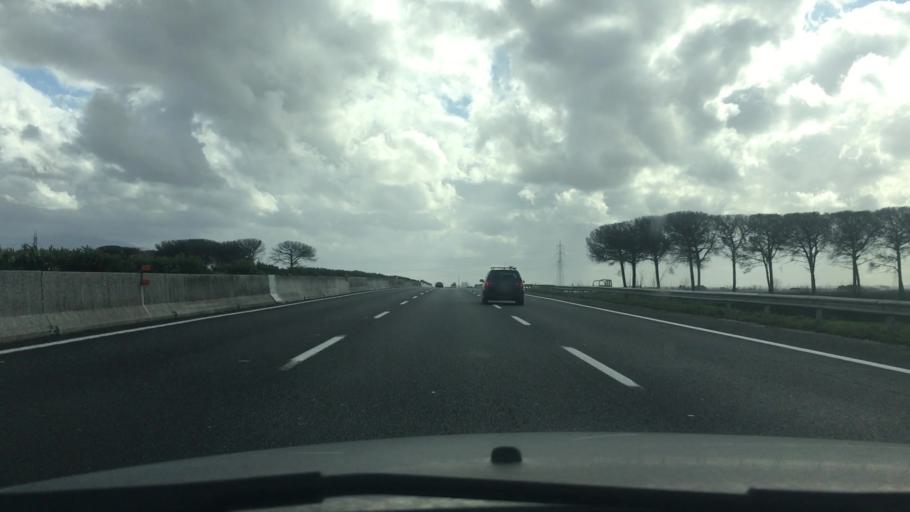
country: IT
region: Campania
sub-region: Provincia di Napoli
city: Pascarola
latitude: 40.9879
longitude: 14.3250
